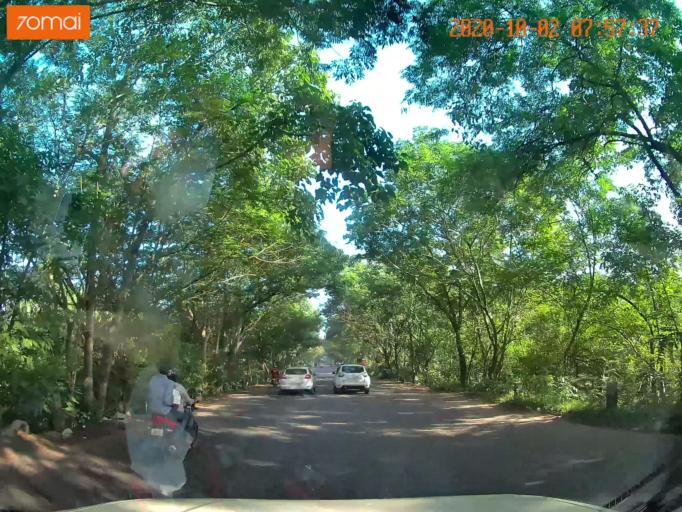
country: IN
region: Kerala
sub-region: Kozhikode
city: Ferokh
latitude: 11.2008
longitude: 75.8669
